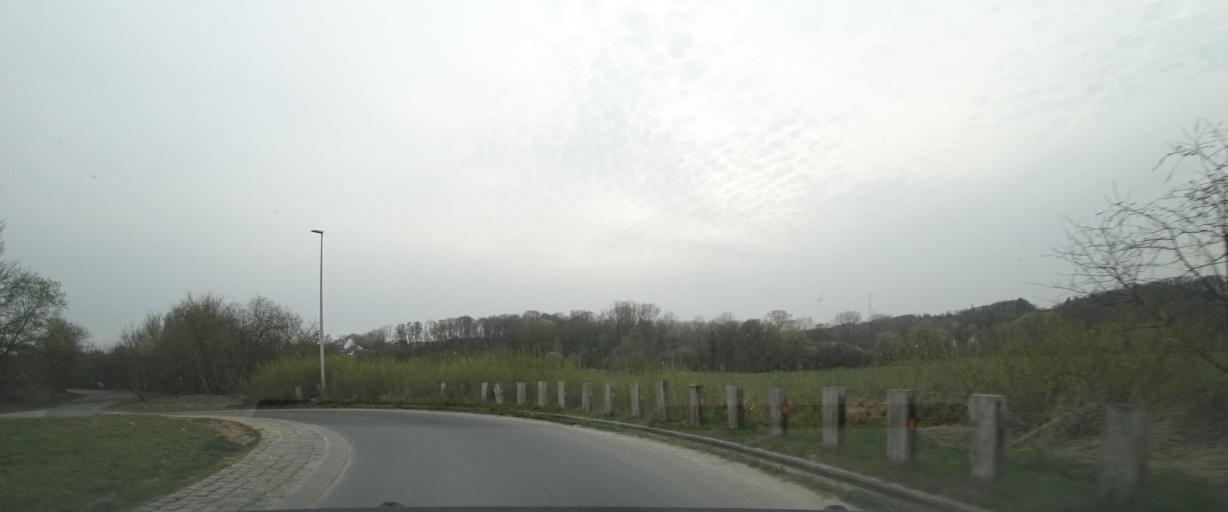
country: BE
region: Wallonia
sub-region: Province du Brabant Wallon
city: Ottignies
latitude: 50.6792
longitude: 4.5532
